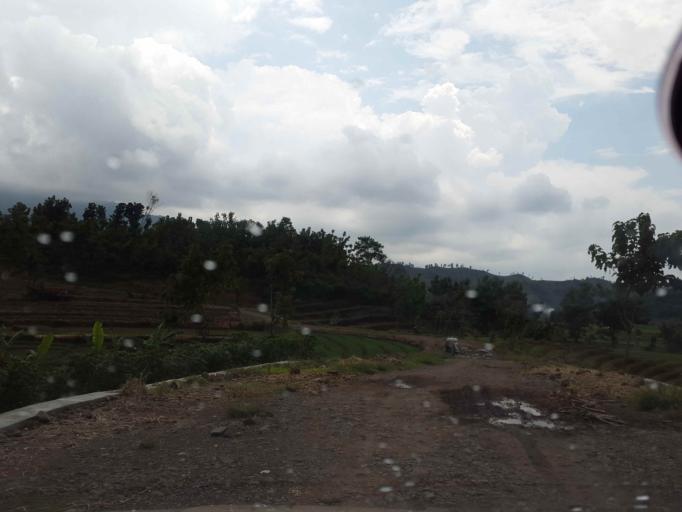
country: ID
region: Central Java
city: Pamedaran
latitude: -7.0977
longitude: 108.8927
